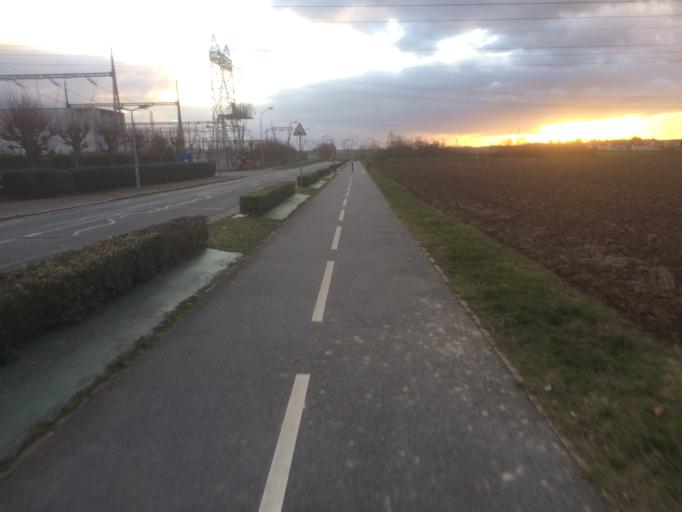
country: FR
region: Ile-de-France
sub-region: Departement de l'Essonne
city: Villejust
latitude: 48.6775
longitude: 2.2292
